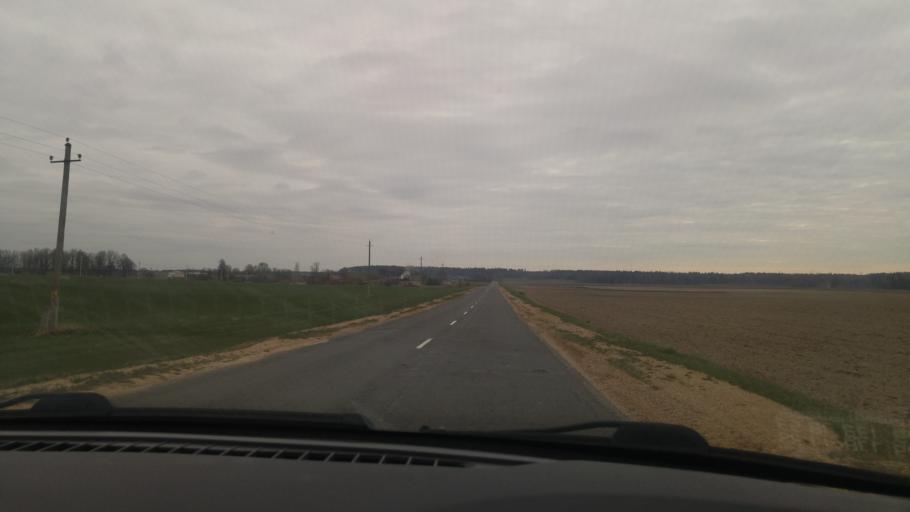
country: BY
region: Minsk
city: Chervyen'
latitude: 53.7228
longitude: 28.2628
